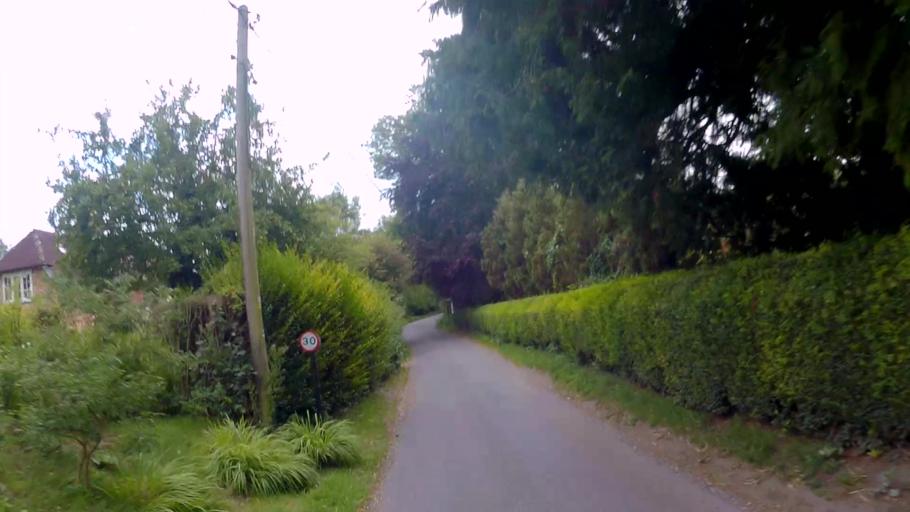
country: GB
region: England
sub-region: Hampshire
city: Kings Worthy
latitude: 51.1543
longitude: -1.3244
